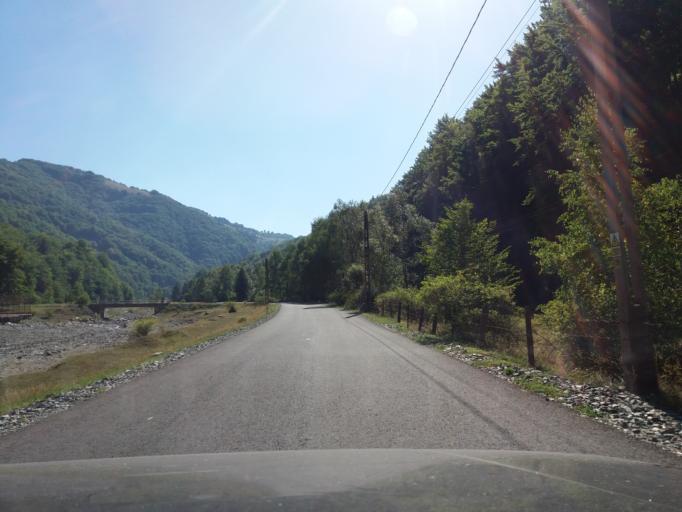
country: RO
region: Hunedoara
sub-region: Oras Petrila
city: Petrila
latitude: 45.4160
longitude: 23.4461
